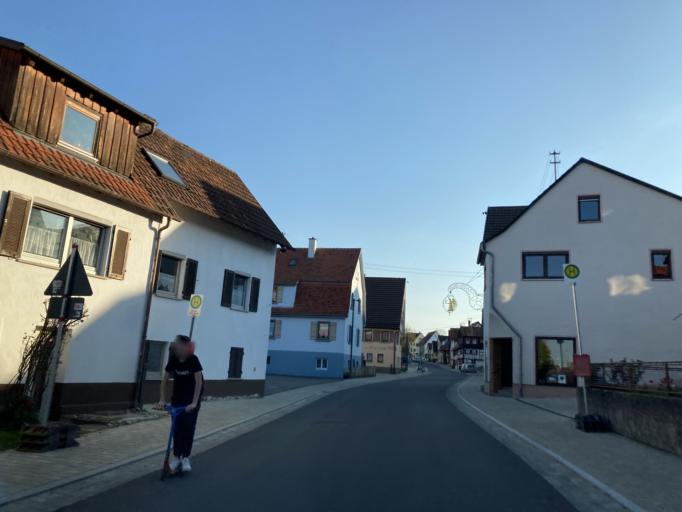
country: DE
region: Baden-Wuerttemberg
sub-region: Tuebingen Region
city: Nehren
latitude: 48.4312
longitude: 9.0693
